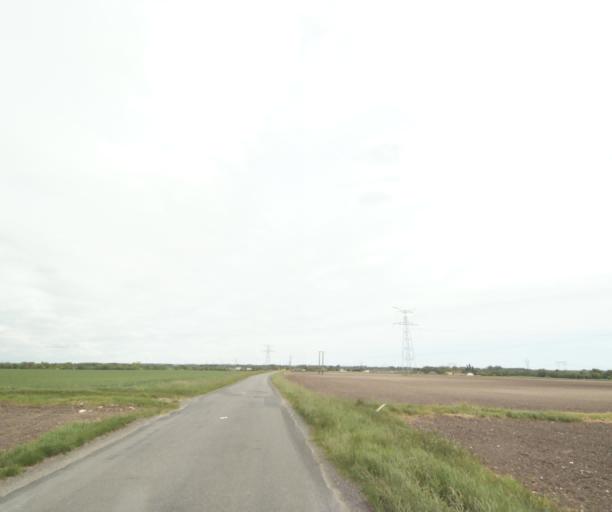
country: FR
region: Poitou-Charentes
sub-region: Departement de la Charente-Maritime
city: Les Gonds
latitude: 45.6878
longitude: -0.6069
